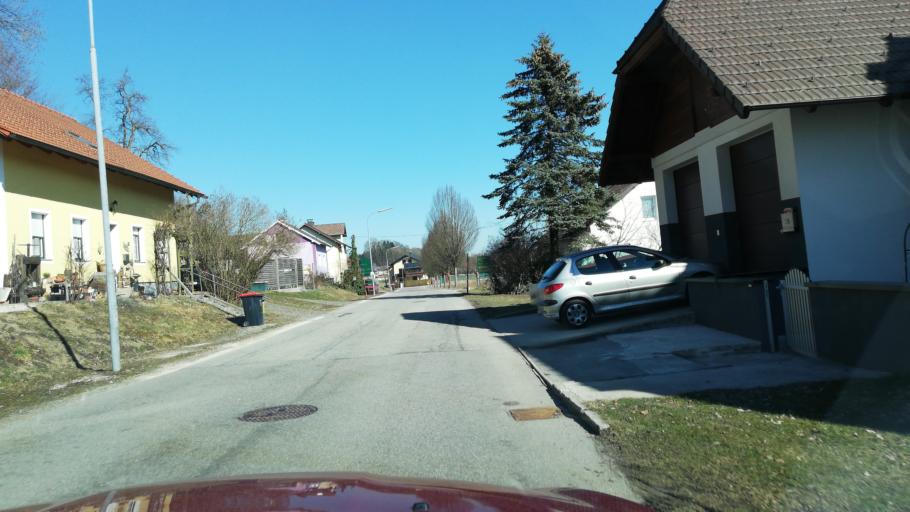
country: AT
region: Upper Austria
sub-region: Politischer Bezirk Vocklabruck
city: Redlham
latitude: 48.0227
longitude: 13.7250
